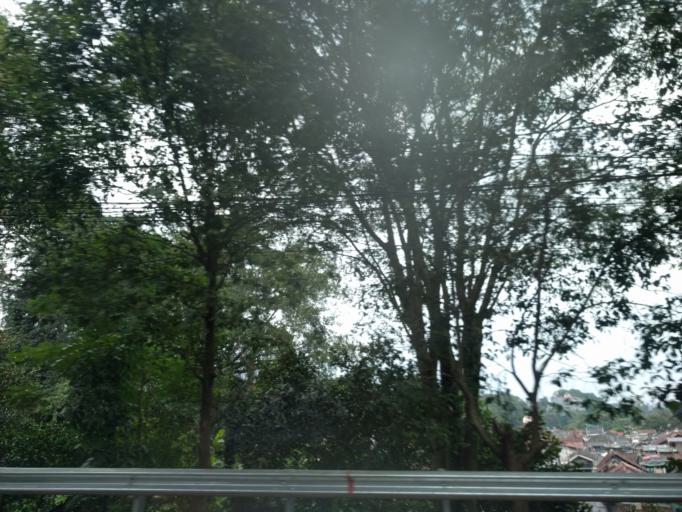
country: ID
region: West Java
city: Bogor
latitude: -6.5931
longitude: 106.7991
